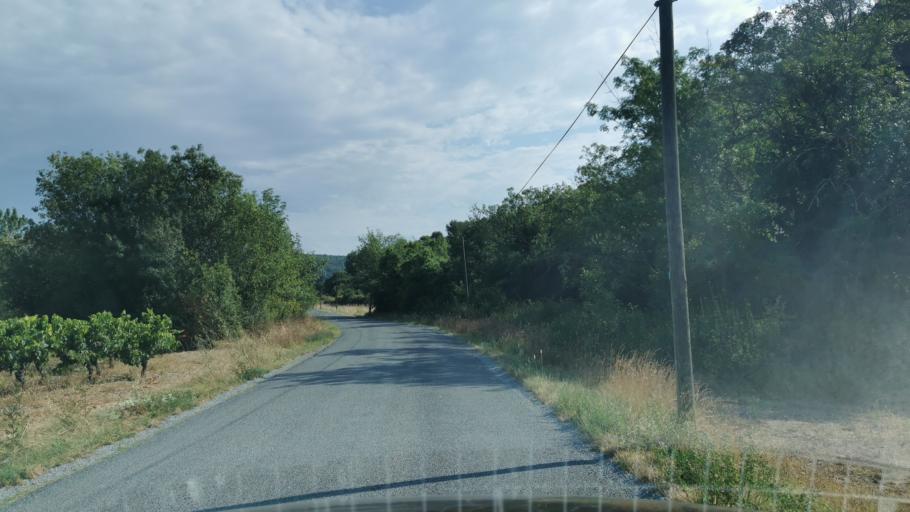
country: FR
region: Languedoc-Roussillon
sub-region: Departement de l'Aude
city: Bize-Minervois
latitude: 43.3367
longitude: 2.8768
